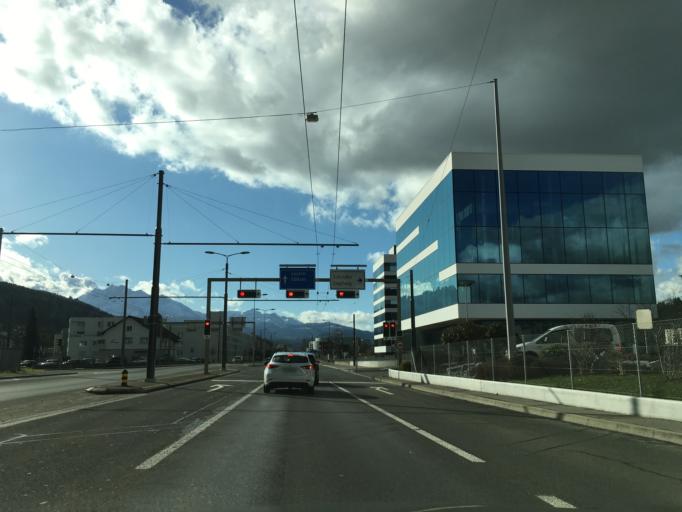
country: CH
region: Lucerne
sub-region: Lucerne-Land District
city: Buchrain
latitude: 47.0891
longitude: 8.3531
